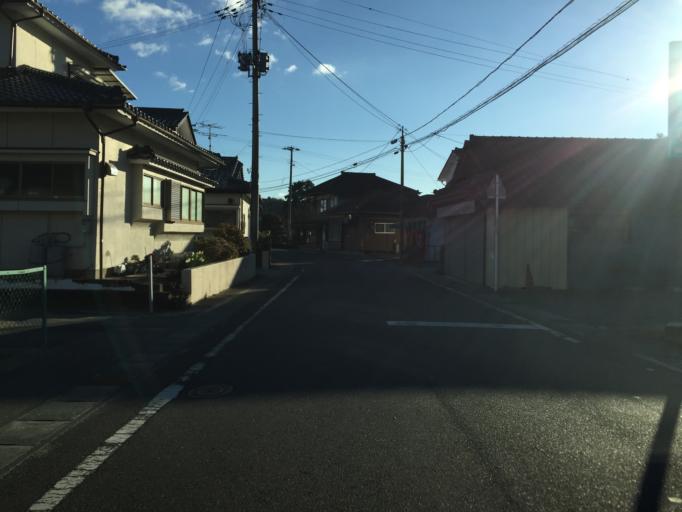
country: JP
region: Fukushima
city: Iwaki
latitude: 37.1295
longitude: 140.8608
